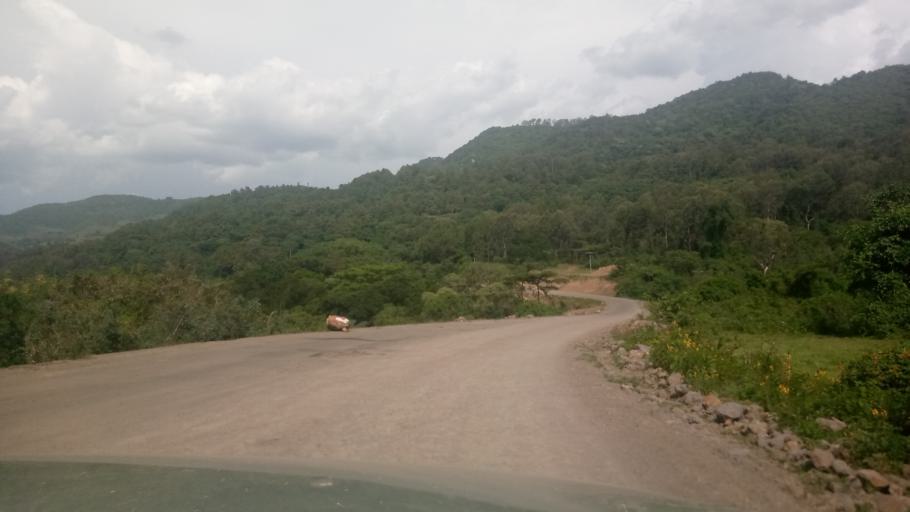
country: ET
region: Oromiya
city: Agaro
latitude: 8.0438
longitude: 36.4666
